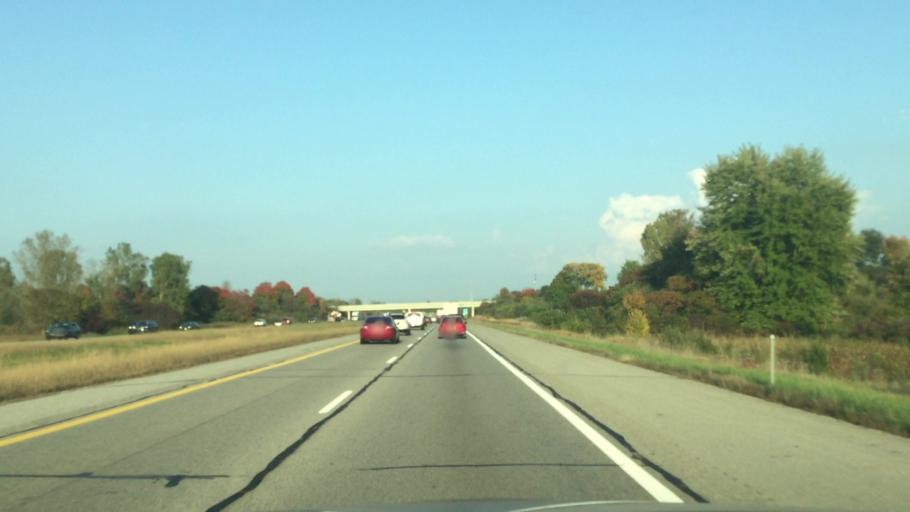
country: US
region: Michigan
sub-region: Wayne County
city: Plymouth
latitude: 42.3656
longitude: -83.5539
